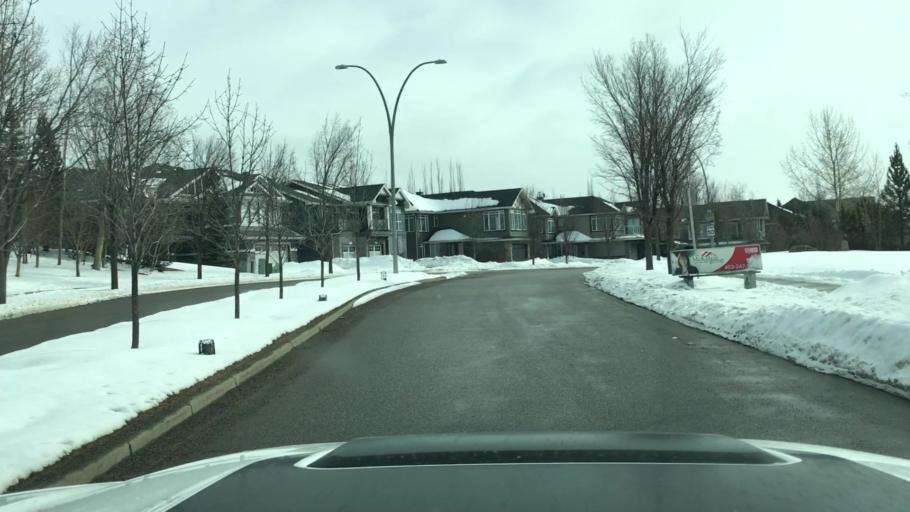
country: CA
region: Alberta
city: Calgary
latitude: 51.1486
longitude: -114.2337
